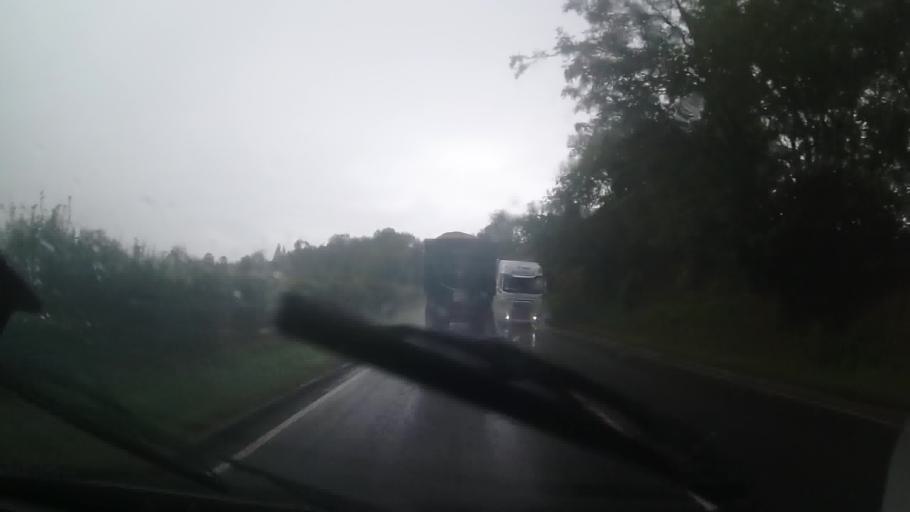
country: GB
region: England
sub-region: Worcestershire
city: Evesham
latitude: 52.1251
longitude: -1.9954
